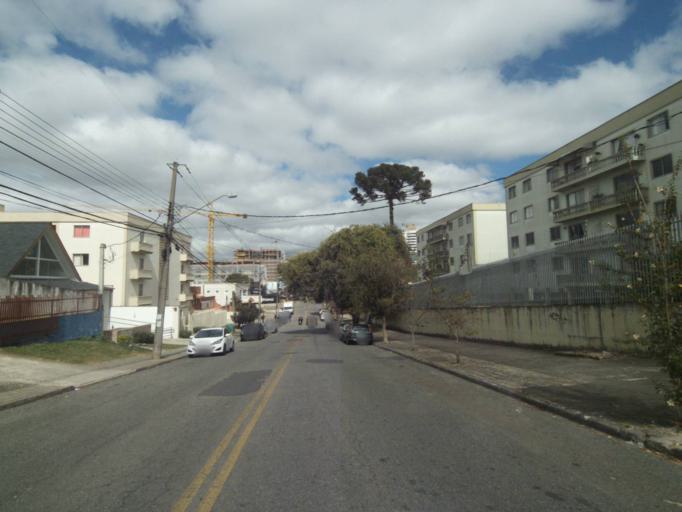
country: BR
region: Parana
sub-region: Curitiba
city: Curitiba
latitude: -25.4643
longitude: -49.2882
